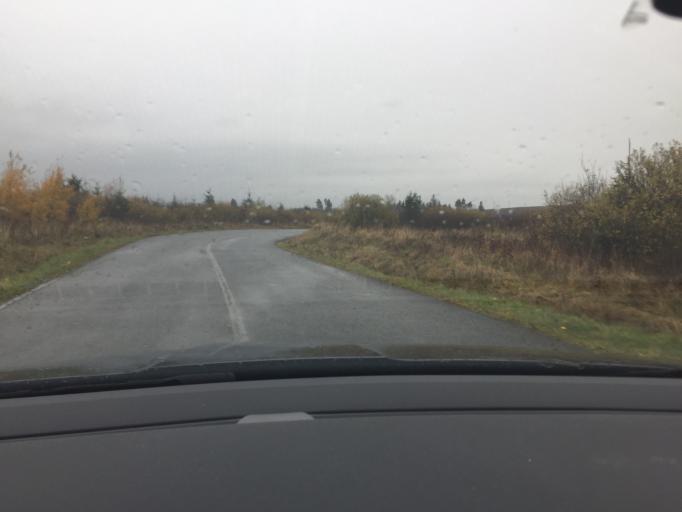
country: SK
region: Presovsky
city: Spisska Bela
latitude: 49.2019
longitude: 20.3757
